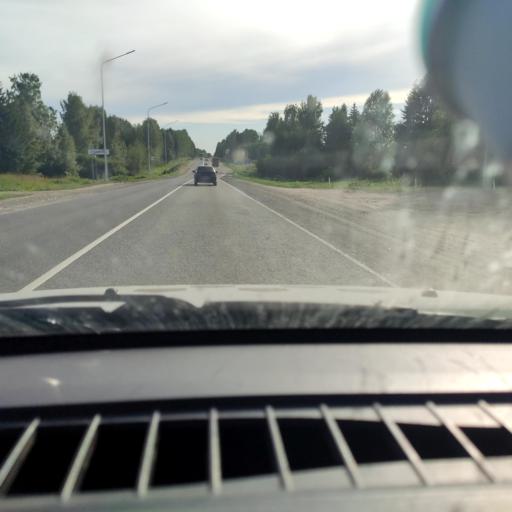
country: RU
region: Kirov
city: Vakhrushi
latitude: 58.6395
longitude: 49.8448
